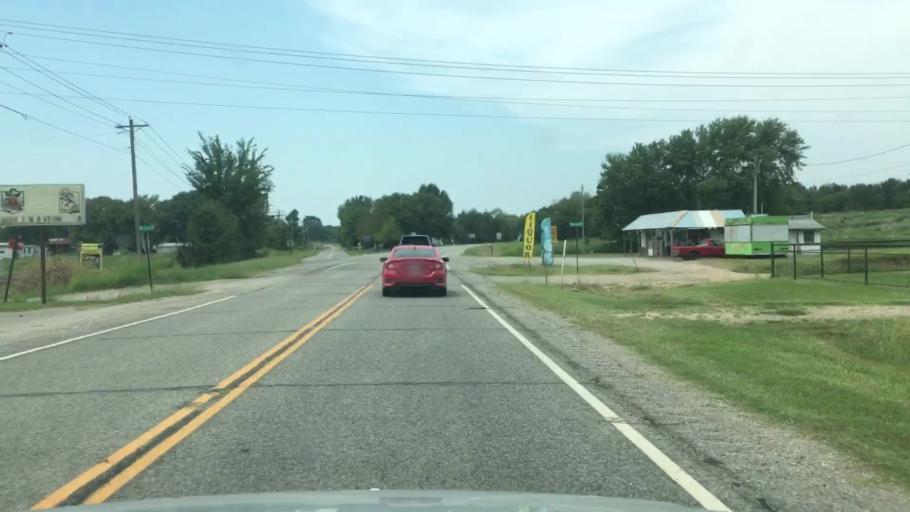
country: US
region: Oklahoma
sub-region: Muskogee County
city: Fort Gibson
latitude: 35.9333
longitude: -95.1537
